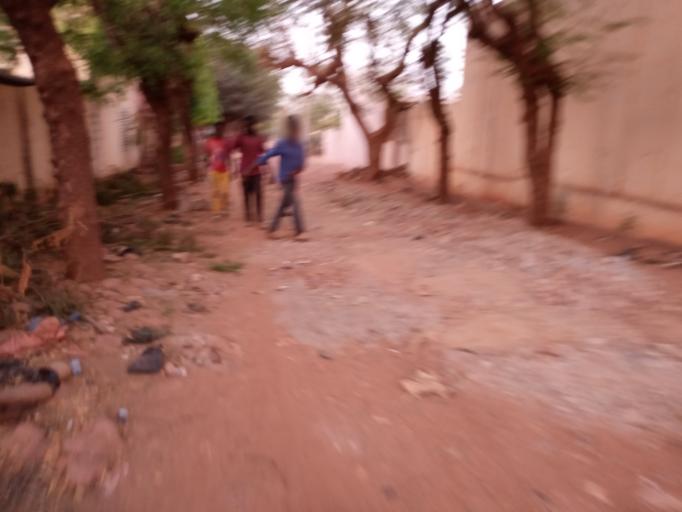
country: ML
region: Bamako
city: Bamako
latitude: 12.5814
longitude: -7.9512
